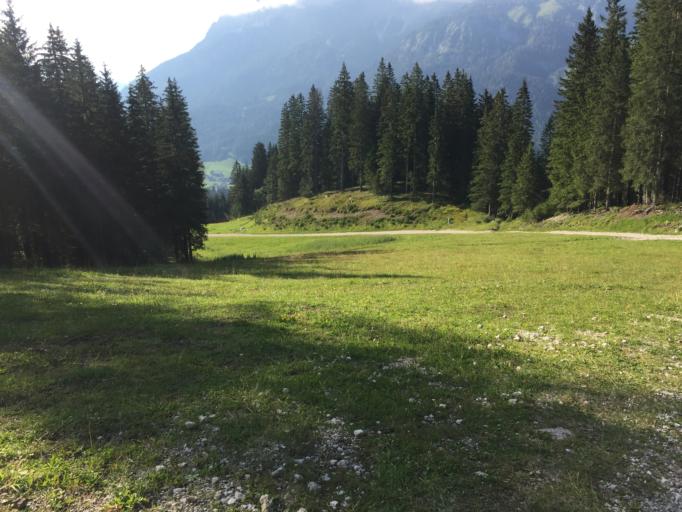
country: IT
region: Veneto
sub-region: Provincia di Belluno
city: Granvilla
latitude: 46.5582
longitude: 12.7182
